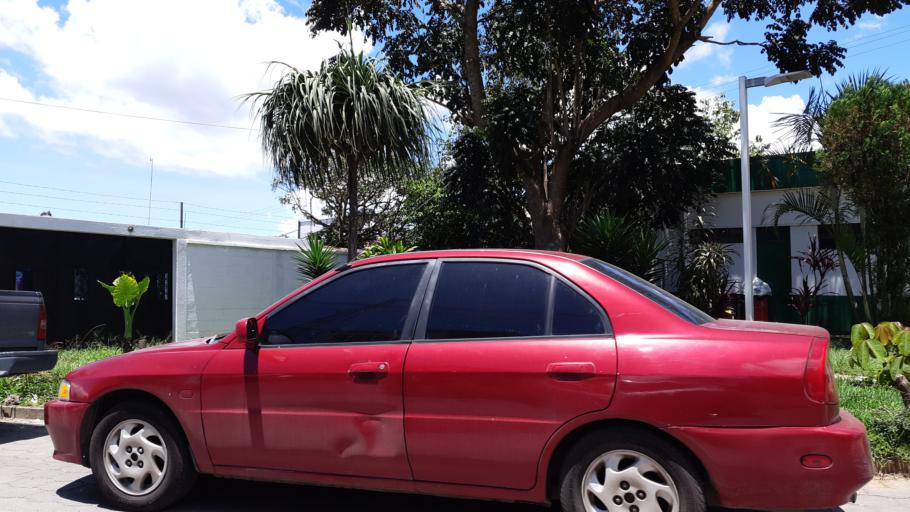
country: GT
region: Chimaltenango
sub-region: Municipio de Chimaltenango
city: Chimaltenango
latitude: 14.6613
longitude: -90.8332
